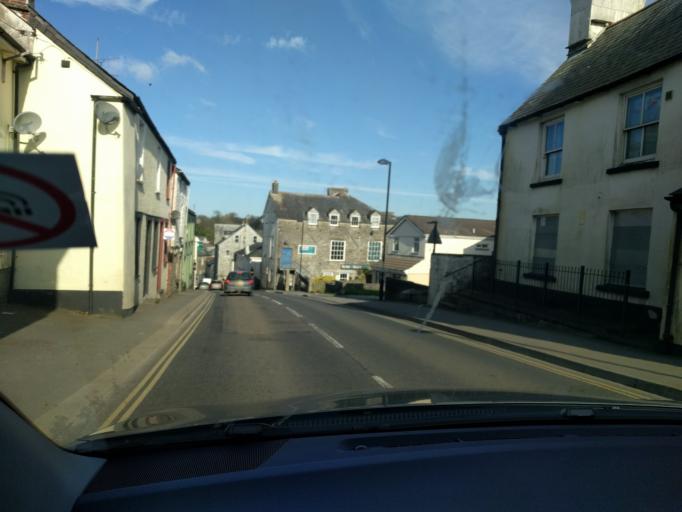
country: GB
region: England
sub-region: Cornwall
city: Camelford
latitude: 50.6208
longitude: -4.6797
